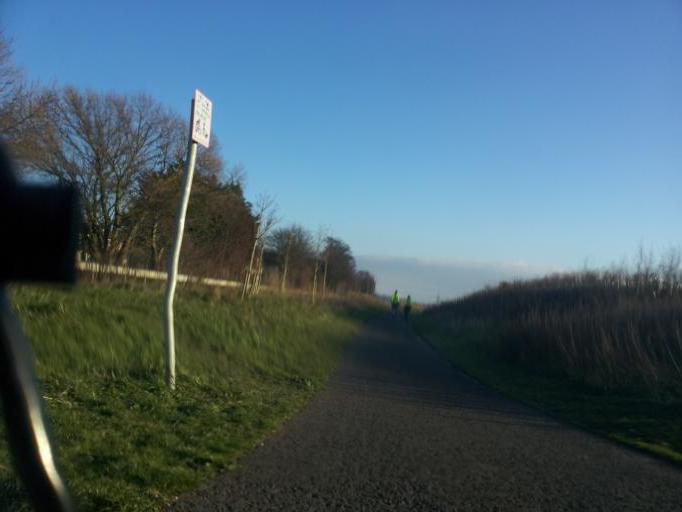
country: GB
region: England
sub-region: Kent
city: Gravesend
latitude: 51.4134
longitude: 0.3710
